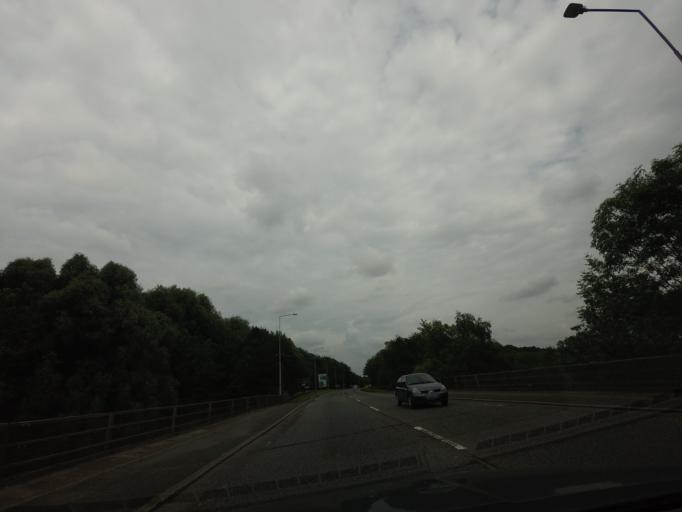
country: GB
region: England
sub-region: Telford and Wrekin
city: Madeley
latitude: 52.6459
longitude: -2.4470
